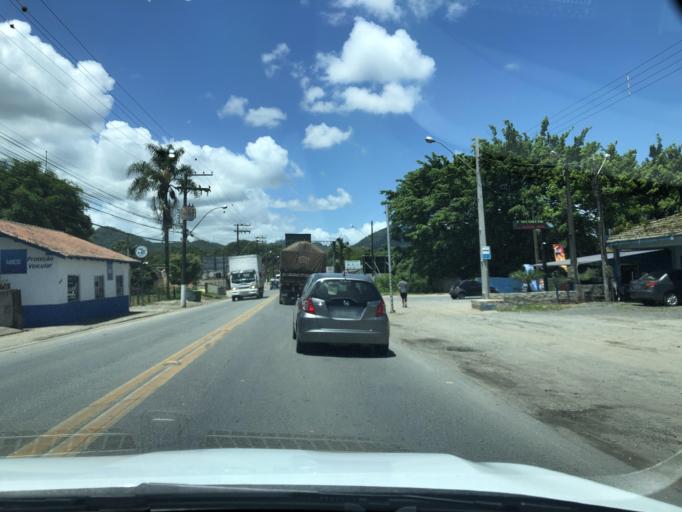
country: BR
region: Santa Catarina
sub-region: Sao Francisco Do Sul
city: Sao Francisco do Sul
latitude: -26.2717
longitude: -48.6416
